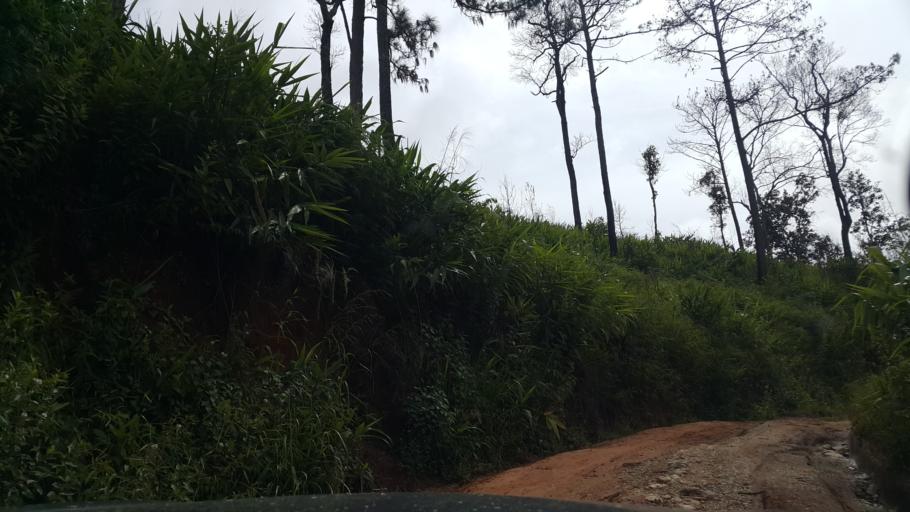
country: TH
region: Chiang Mai
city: Samoeng
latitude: 18.8705
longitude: 98.4980
